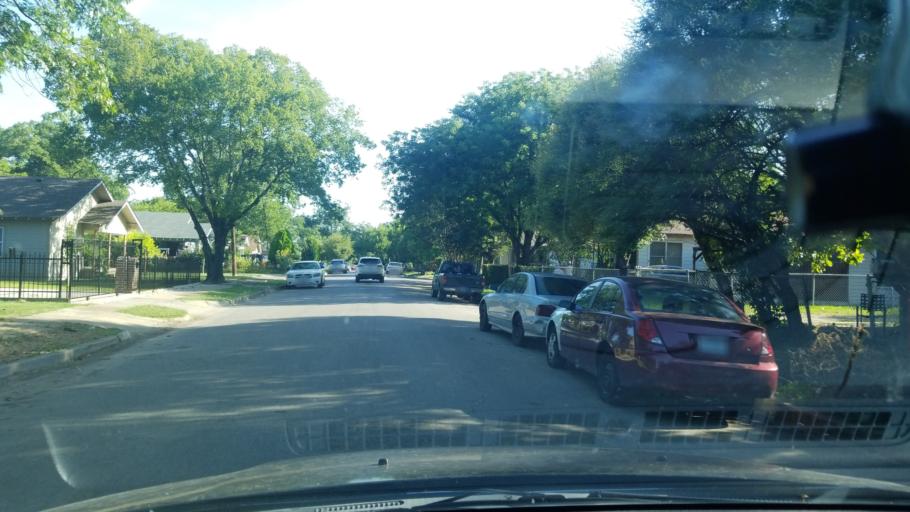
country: US
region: Texas
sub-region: Dallas County
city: Dallas
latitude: 32.7173
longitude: -96.8121
